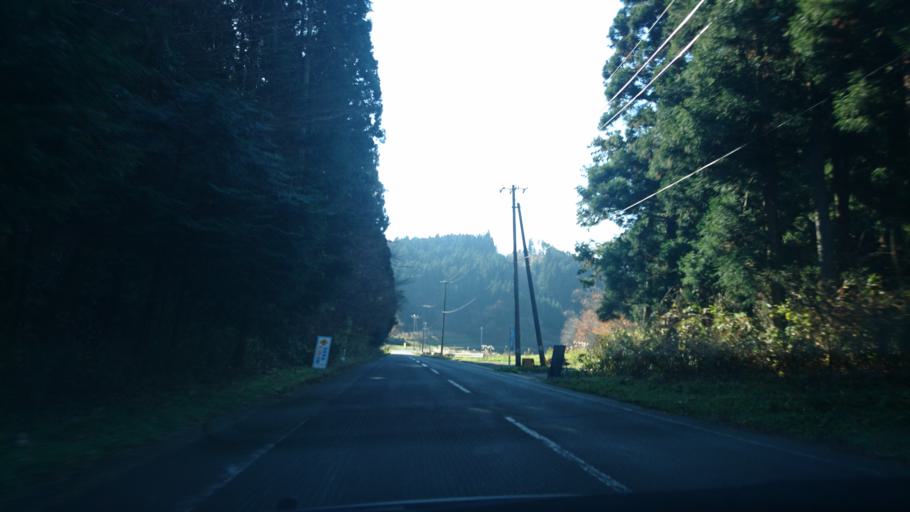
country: JP
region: Iwate
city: Ichinoseki
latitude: 38.9024
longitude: 141.4091
